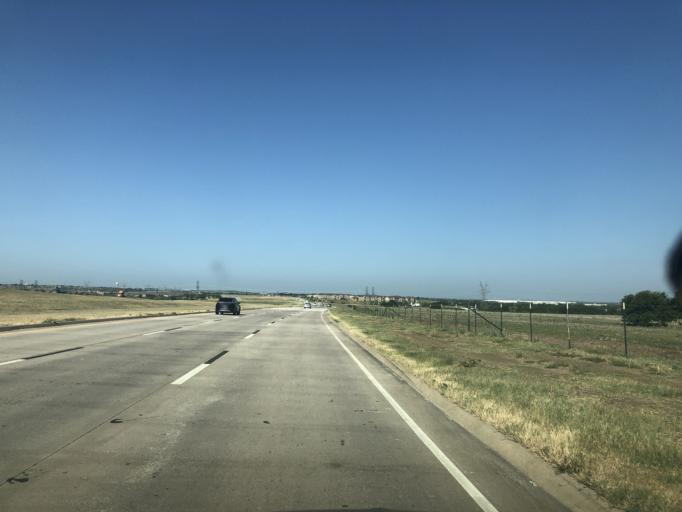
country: US
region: Texas
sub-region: Tarrant County
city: Keller
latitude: 32.9710
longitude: -97.2829
